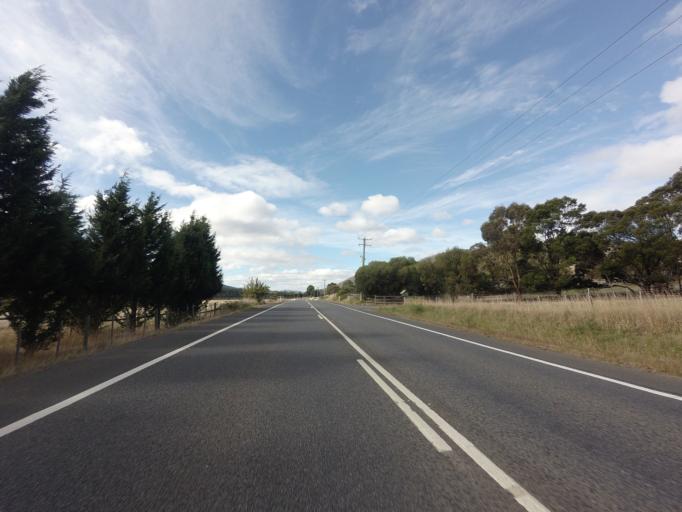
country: AU
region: Tasmania
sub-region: Derwent Valley
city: New Norfolk
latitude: -42.7769
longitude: 147.1151
